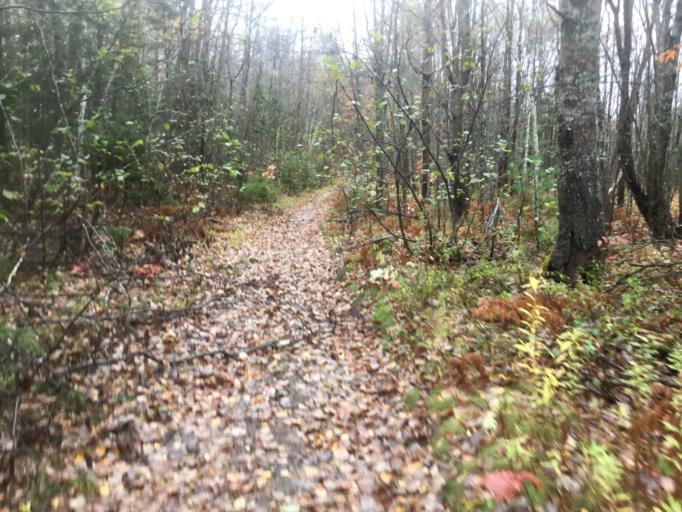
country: CA
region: Nova Scotia
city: New Glasgow
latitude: 45.5492
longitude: -62.6795
